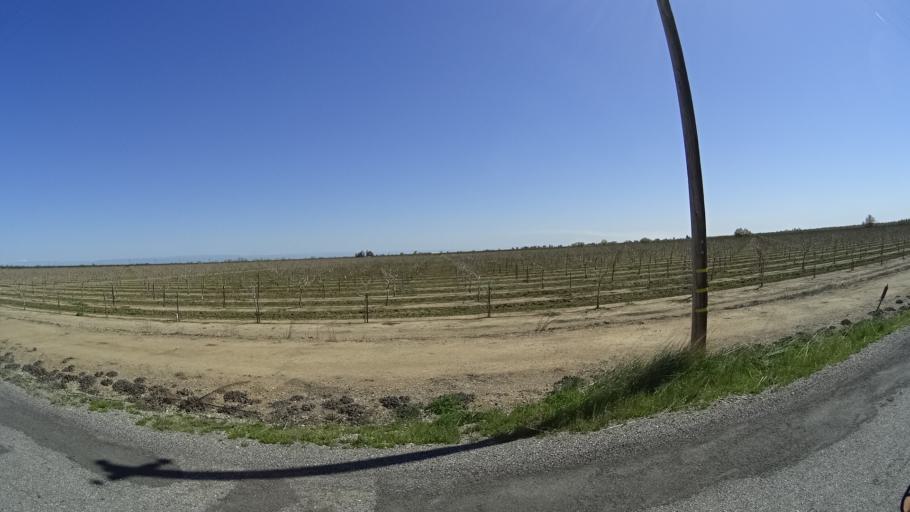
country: US
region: California
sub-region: Glenn County
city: Willows
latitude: 39.6347
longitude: -122.2340
